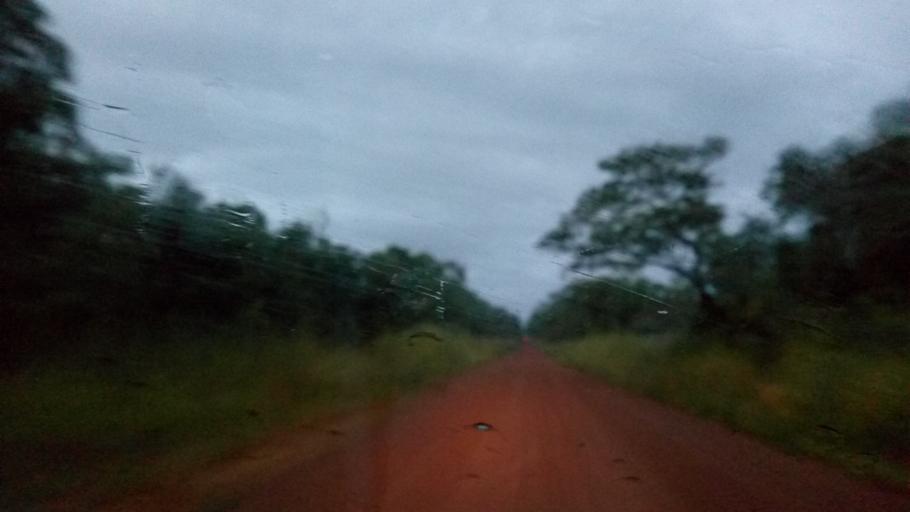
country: ZM
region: Luapula
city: Nchelenge
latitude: -9.8189
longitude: 28.1373
